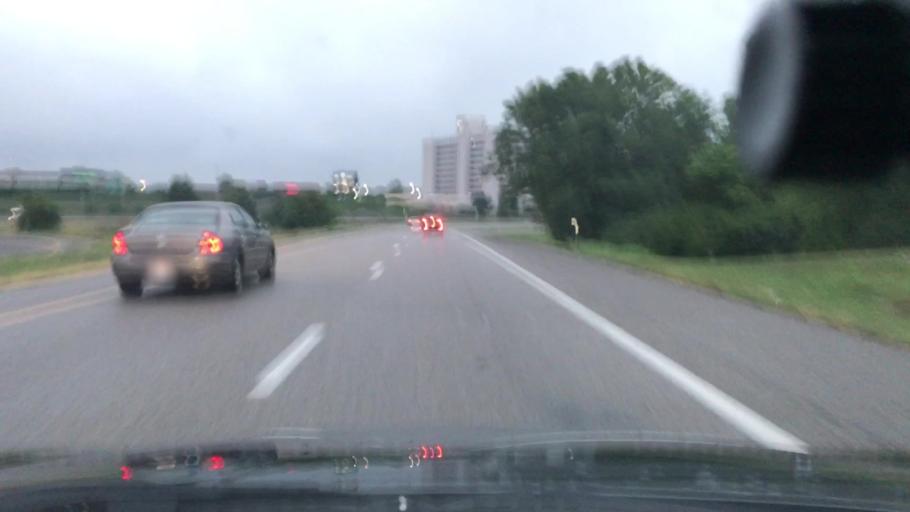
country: US
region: Missouri
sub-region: Saint Louis County
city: Maryland Heights
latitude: 38.6964
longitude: -90.4526
